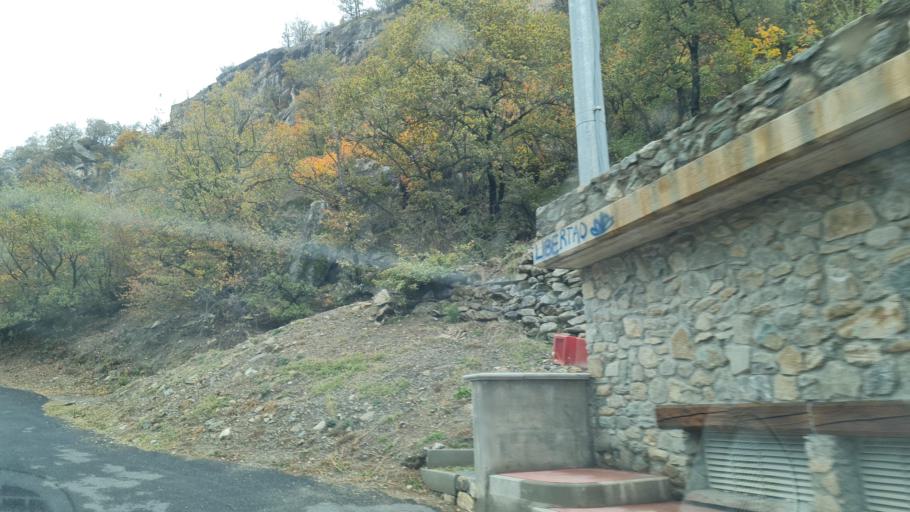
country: IT
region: Piedmont
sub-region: Provincia di Torino
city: Bussoleno
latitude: 45.1483
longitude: 7.1394
